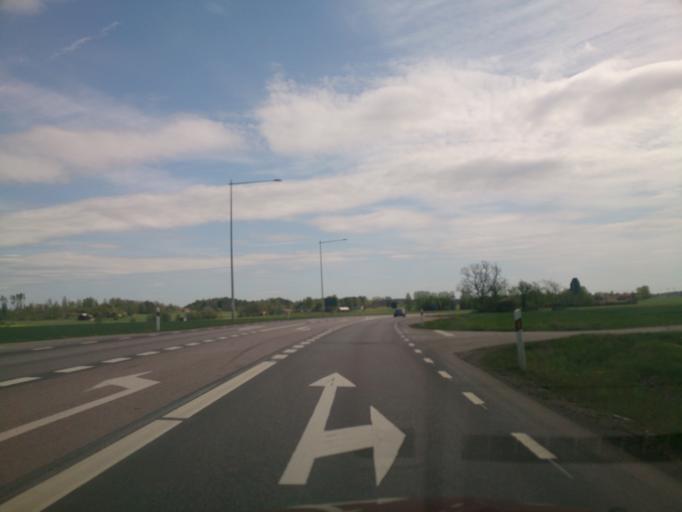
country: SE
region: OEstergoetland
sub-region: Linkopings Kommun
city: Linghem
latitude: 58.4010
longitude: 15.7518
